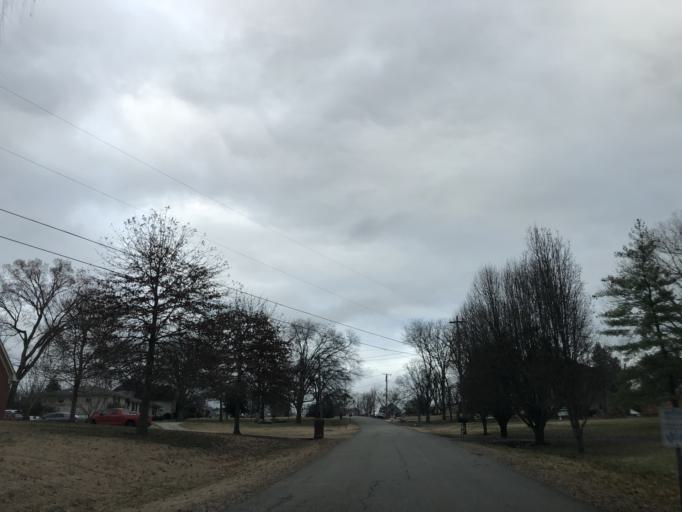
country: US
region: Tennessee
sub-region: Davidson County
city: Goodlettsville
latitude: 36.2957
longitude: -86.6855
